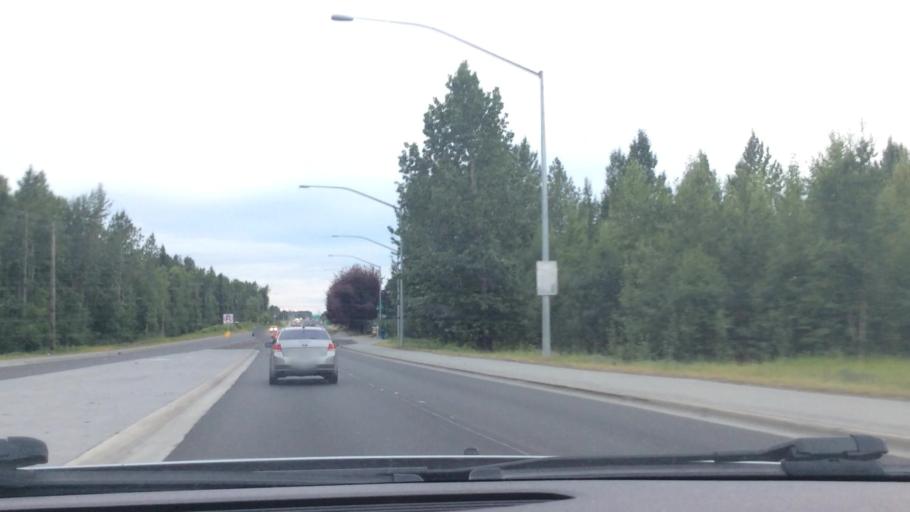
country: US
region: Alaska
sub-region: Anchorage Municipality
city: Anchorage
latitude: 61.1809
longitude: -149.8431
